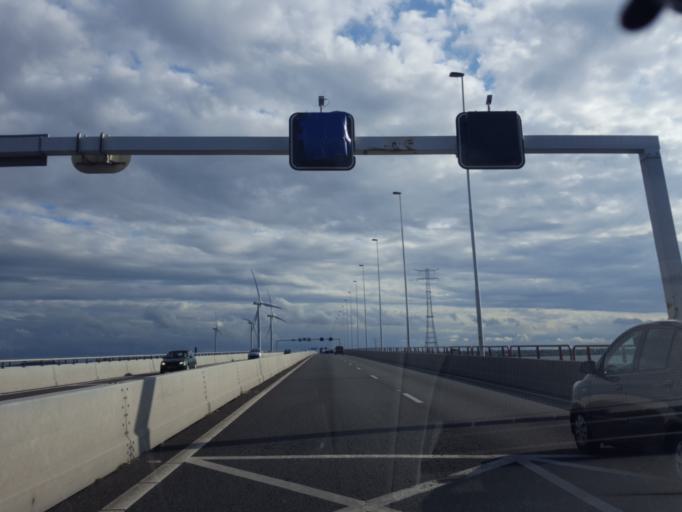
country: NL
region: North Brabant
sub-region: Gemeente Moerdijk
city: Willemstad
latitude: 51.7188
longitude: 4.4026
